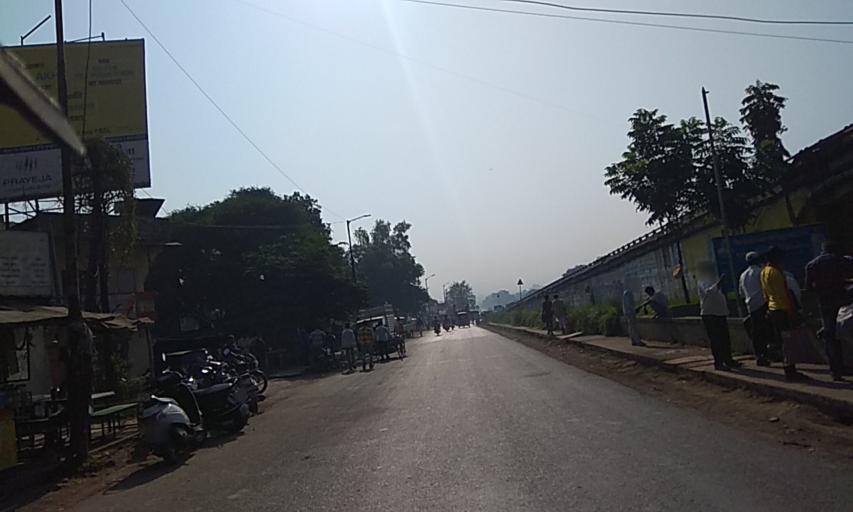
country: IN
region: Maharashtra
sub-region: Pune Division
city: Kharakvasla
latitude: 18.4788
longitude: 73.8059
